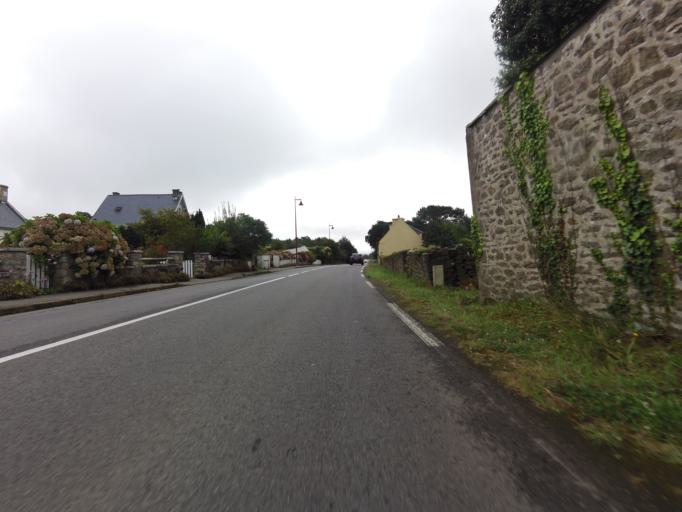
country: FR
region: Brittany
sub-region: Departement du Finistere
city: Plouhinec
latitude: 48.0127
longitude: -4.4759
